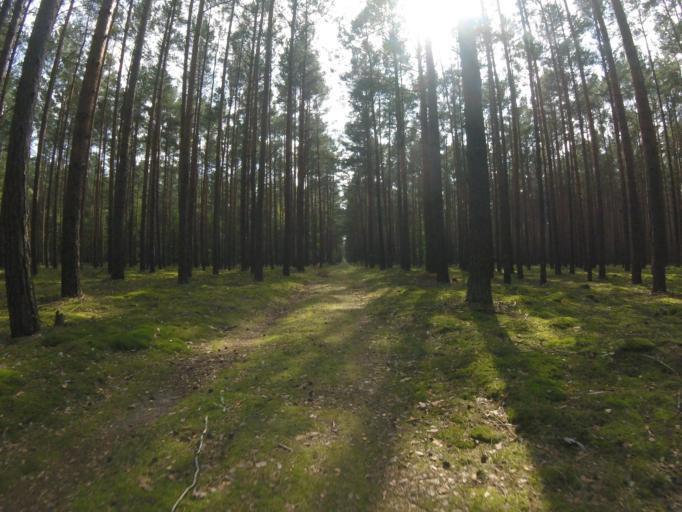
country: DE
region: Brandenburg
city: Gross Koris
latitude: 52.2268
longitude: 13.7560
